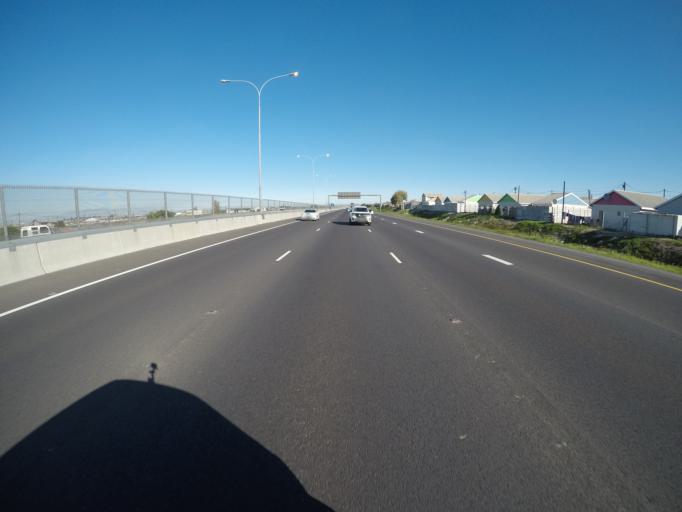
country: ZA
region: Western Cape
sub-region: City of Cape Town
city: Kraaifontein
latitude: -33.9622
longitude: 18.6557
